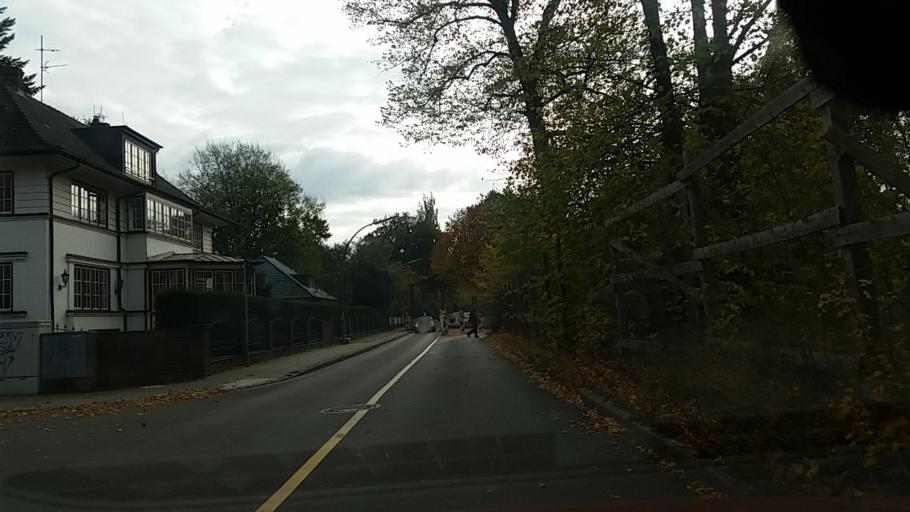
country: DE
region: Hamburg
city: Marienthal
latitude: 53.5641
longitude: 10.0663
